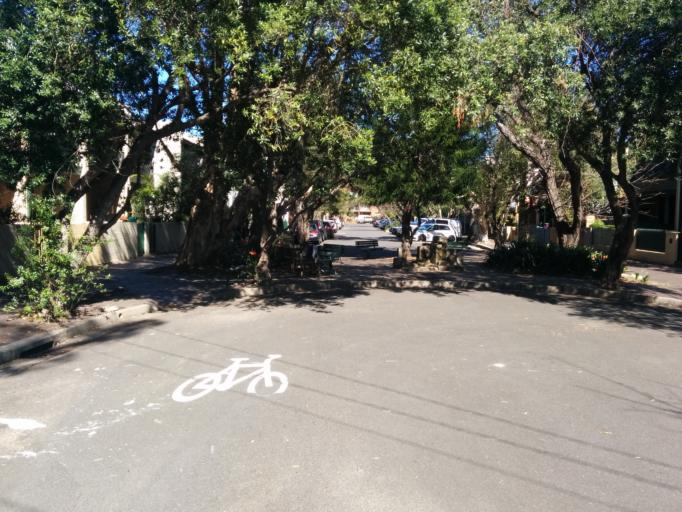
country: AU
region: New South Wales
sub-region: City of Sydney
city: Alexandria
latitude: -33.9058
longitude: 151.1898
